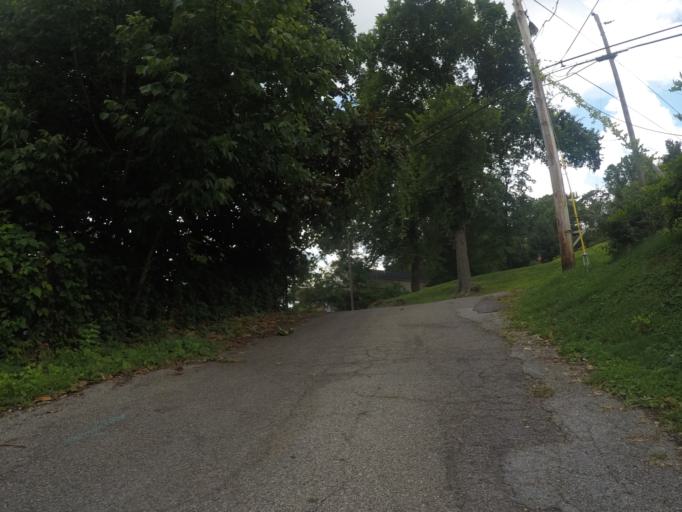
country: US
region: West Virginia
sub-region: Cabell County
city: Huntington
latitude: 38.4210
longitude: -82.3842
